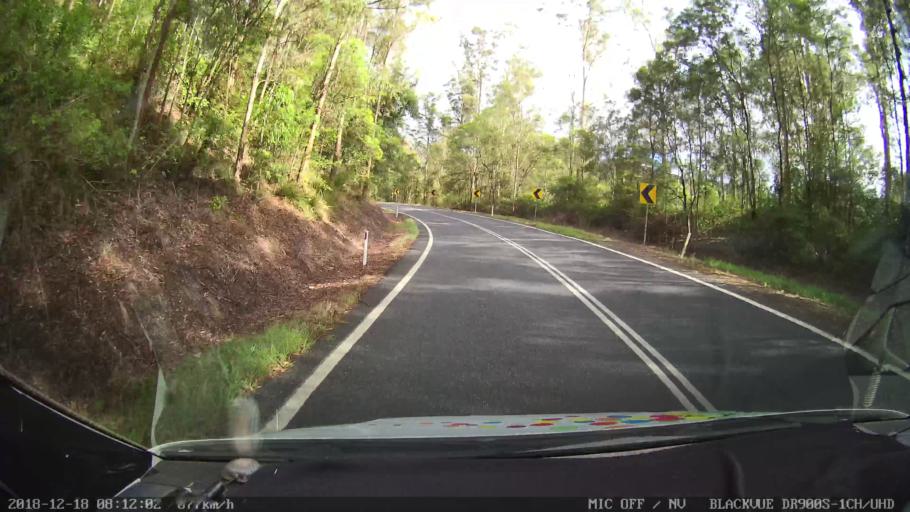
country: AU
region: New South Wales
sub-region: Kyogle
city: Kyogle
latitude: -28.3432
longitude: 152.6705
